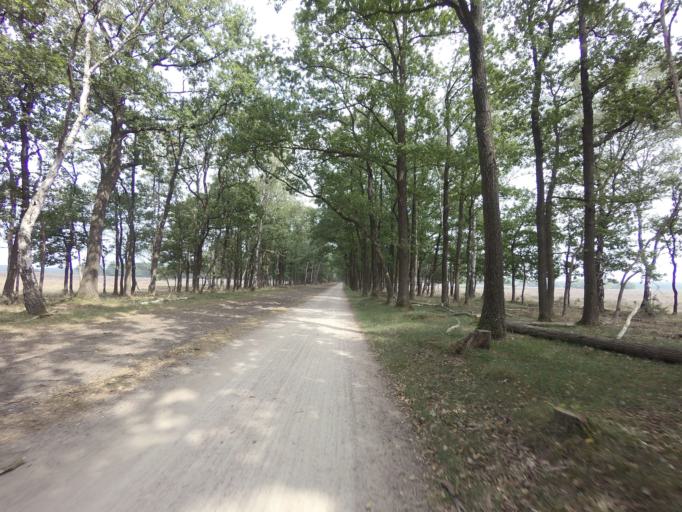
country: NL
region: North Holland
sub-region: Gemeente Bussum
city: Bussum
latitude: 52.2540
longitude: 5.1840
